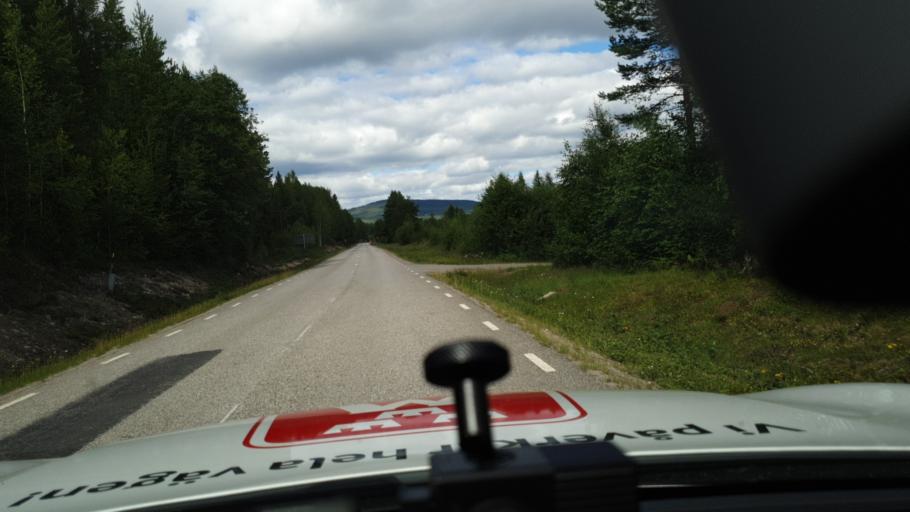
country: NO
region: Hedmark
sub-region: Trysil
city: Innbygda
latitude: 61.0392
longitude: 12.5897
